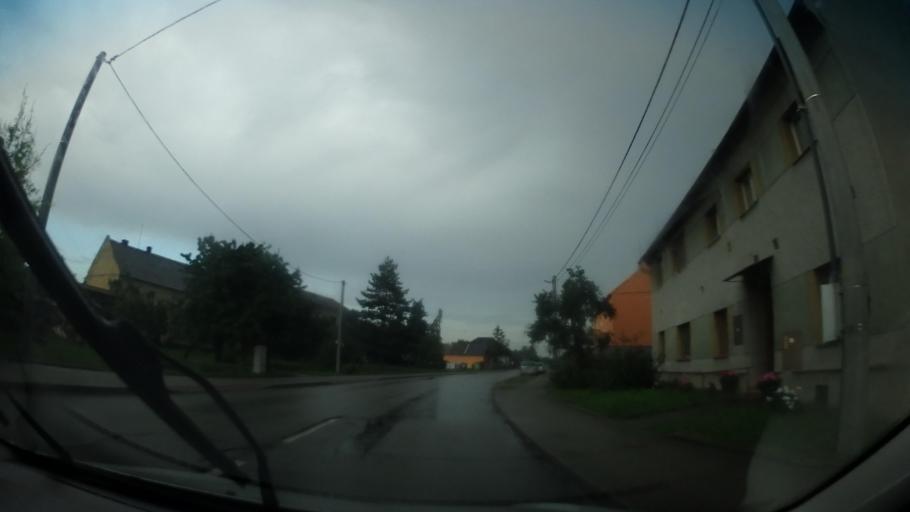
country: CZ
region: Olomoucky
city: Cervenka
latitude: 49.7135
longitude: 17.1066
